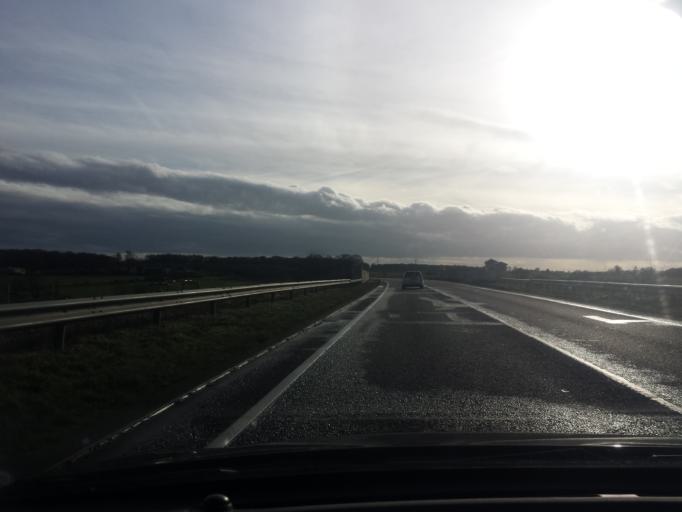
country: GB
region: England
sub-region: Essex
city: Great Bentley
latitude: 51.8526
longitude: 1.1015
